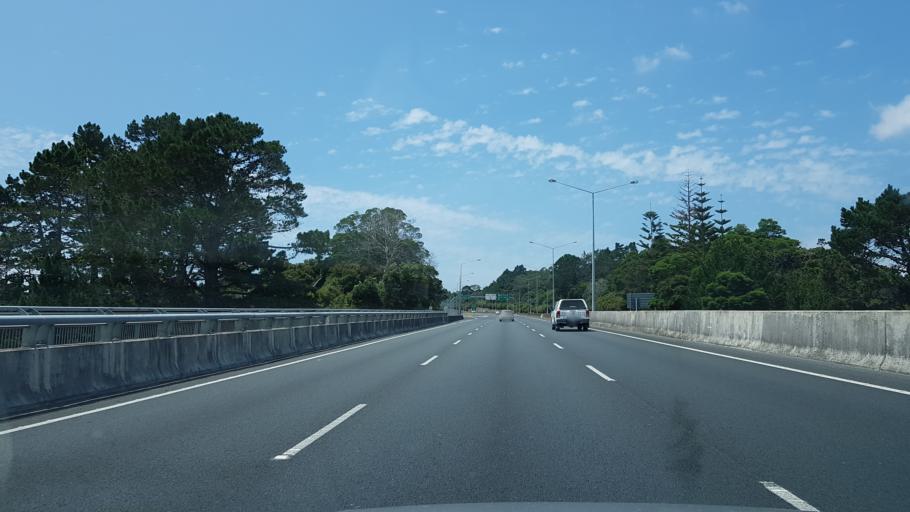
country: NZ
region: Auckland
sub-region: Auckland
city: North Shore
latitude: -36.7846
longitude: 174.6693
